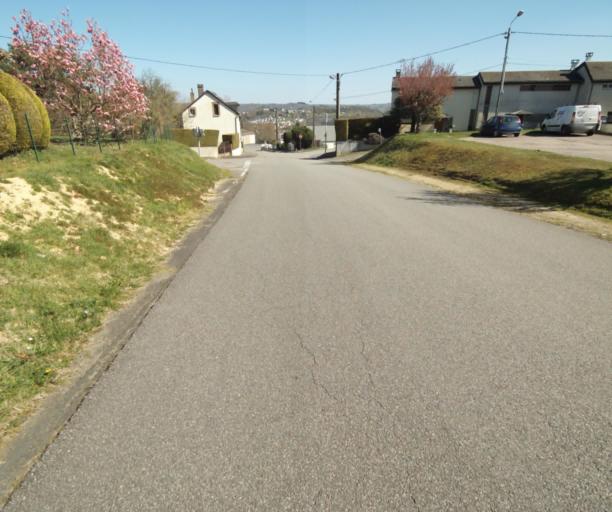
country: FR
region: Limousin
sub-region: Departement de la Correze
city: Tulle
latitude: 45.2589
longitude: 1.7398
